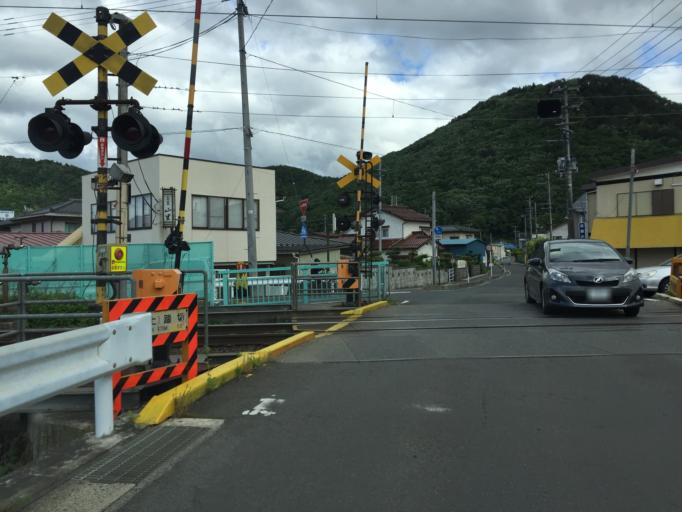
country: JP
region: Fukushima
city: Fukushima-shi
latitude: 37.7773
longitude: 140.4585
